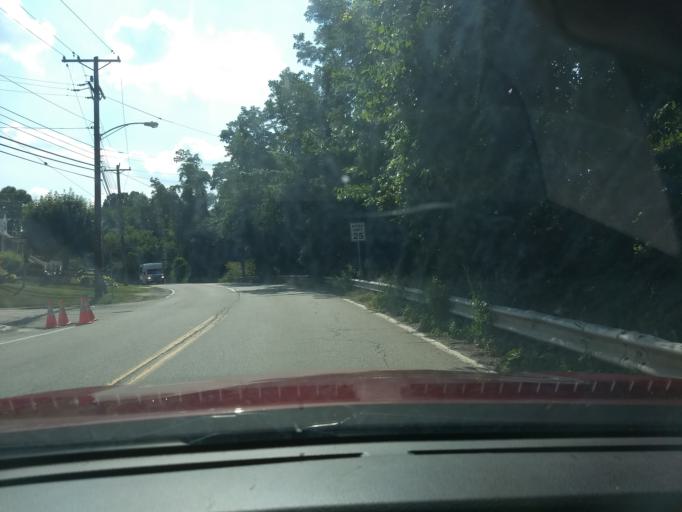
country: US
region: Pennsylvania
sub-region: Allegheny County
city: West Homestead
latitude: 40.3885
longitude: -79.9093
